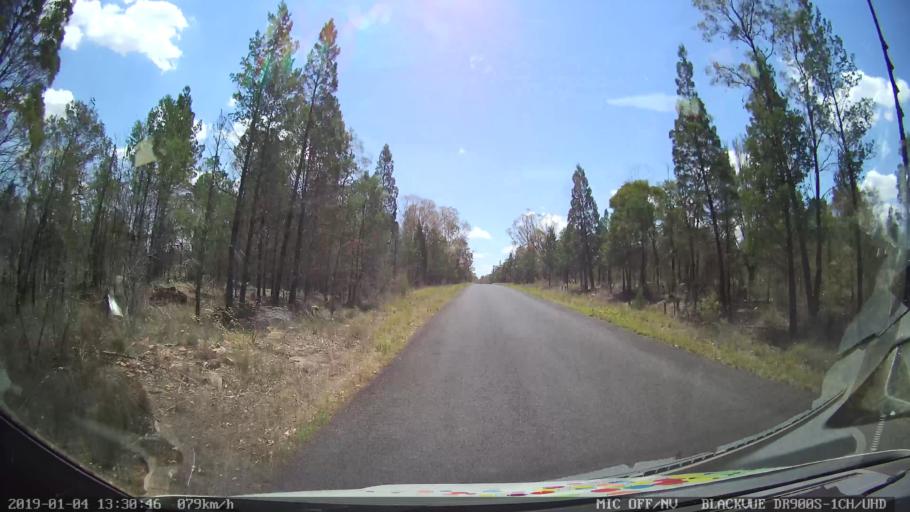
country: AU
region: New South Wales
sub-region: Parkes
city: Peak Hill
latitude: -32.6311
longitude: 148.5492
